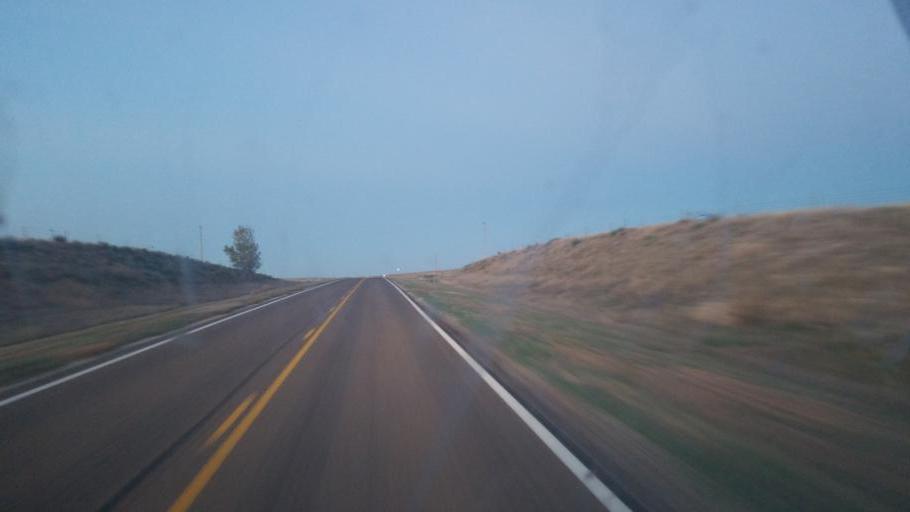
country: US
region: Kansas
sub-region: Wallace County
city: Sharon Springs
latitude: 39.0147
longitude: -101.3557
